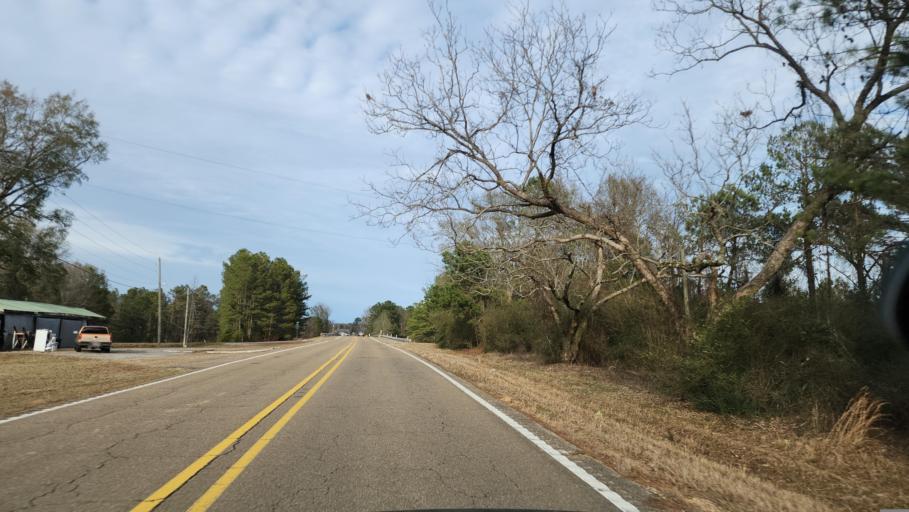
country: US
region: Mississippi
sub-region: Lauderdale County
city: Meridian
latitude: 32.2787
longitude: -88.6983
